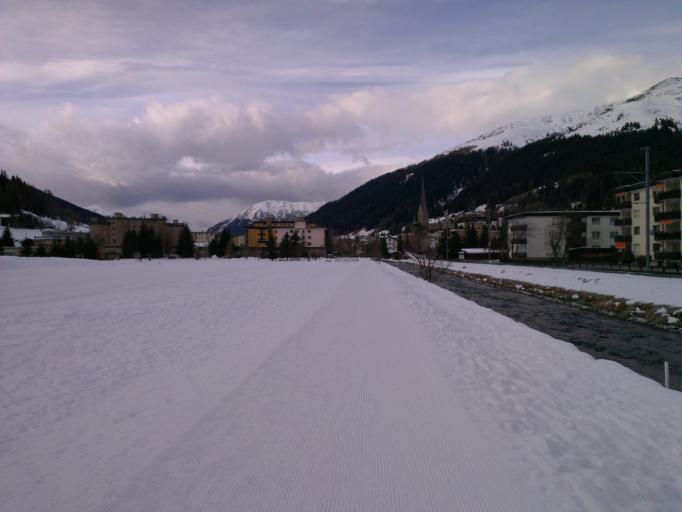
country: CH
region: Grisons
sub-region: Praettigau/Davos District
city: Davos
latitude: 46.7963
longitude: 9.8288
